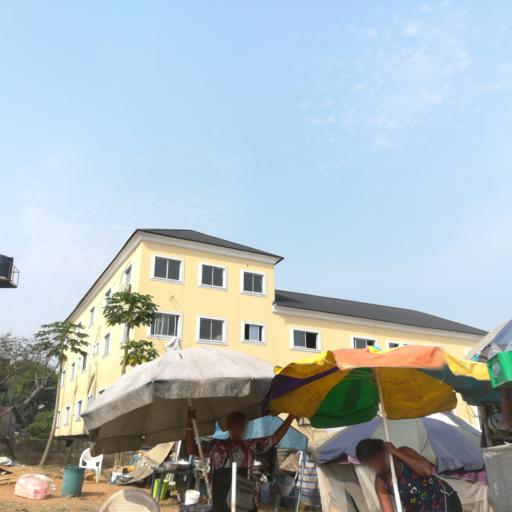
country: NG
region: Rivers
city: Port Harcourt
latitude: 4.8531
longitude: 7.0633
